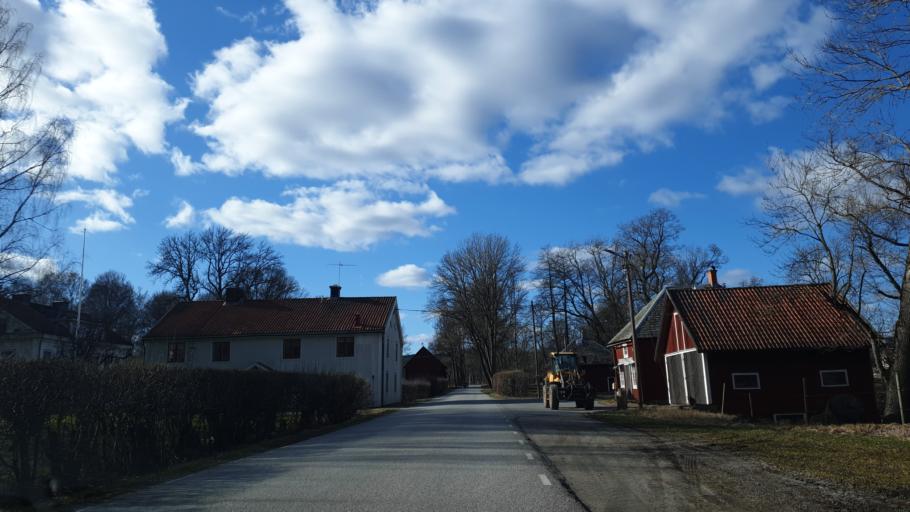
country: SE
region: OErebro
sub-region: Orebro Kommun
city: Garphyttan
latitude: 59.3429
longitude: 15.0140
